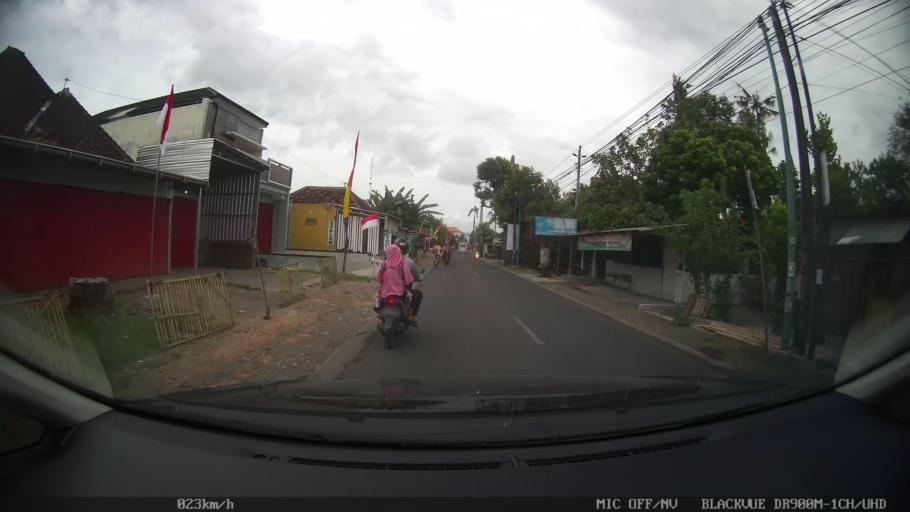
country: ID
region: Daerah Istimewa Yogyakarta
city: Sewon
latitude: -7.8599
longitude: 110.4091
